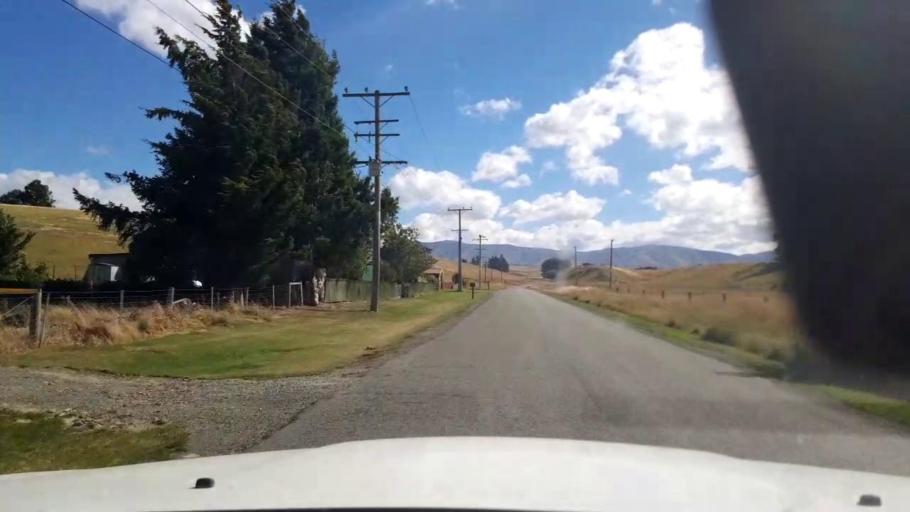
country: NZ
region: Canterbury
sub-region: Timaru District
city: Pleasant Point
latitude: -44.2332
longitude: 170.8753
